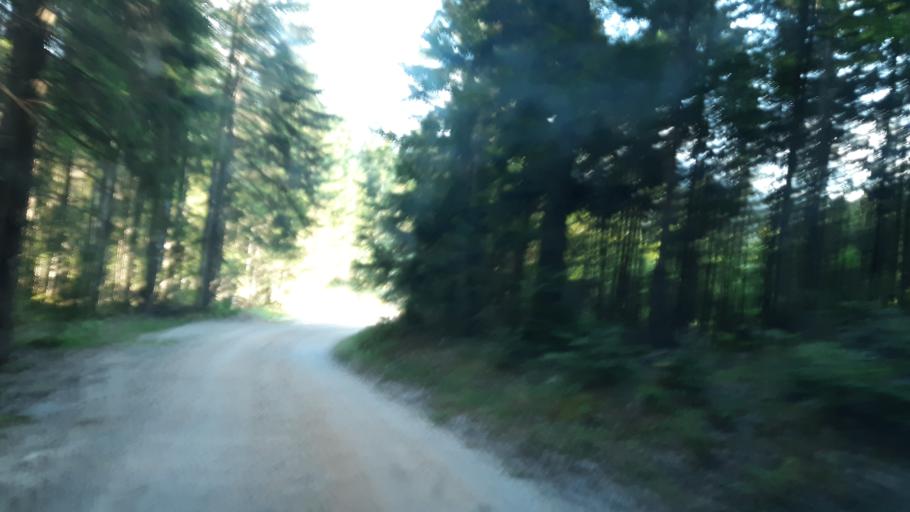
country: SI
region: Dolenjske Toplice
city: Dolenjske Toplice
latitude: 45.7057
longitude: 15.0089
